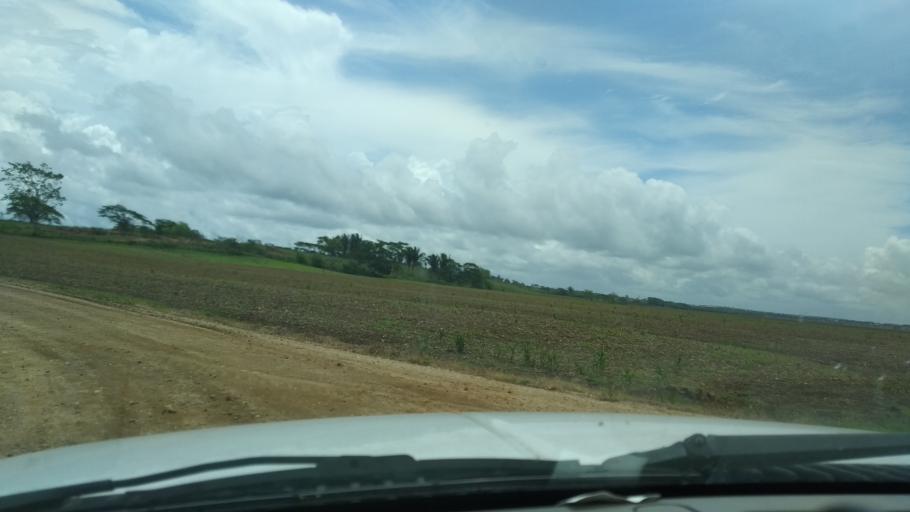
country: BZ
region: Cayo
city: San Ignacio
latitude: 17.2264
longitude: -88.9724
